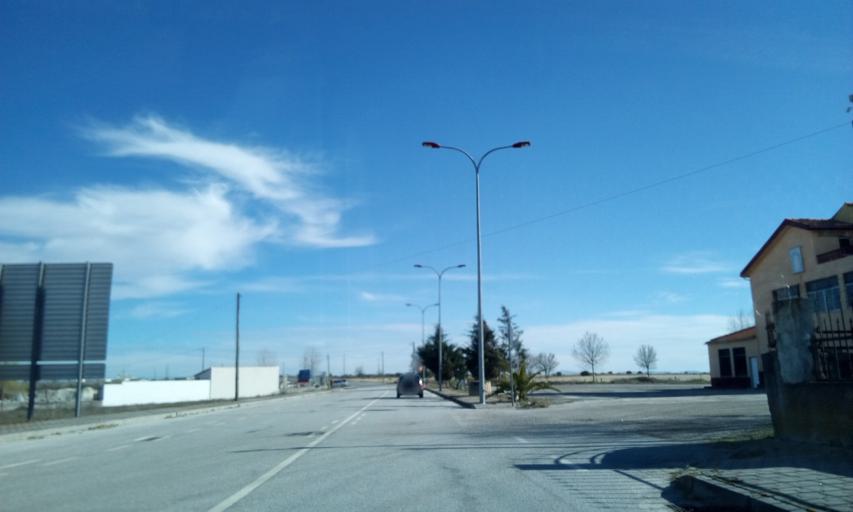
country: ES
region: Castille and Leon
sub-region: Provincia de Salamanca
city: Fuentes de Onoro
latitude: 40.5942
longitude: -6.9917
